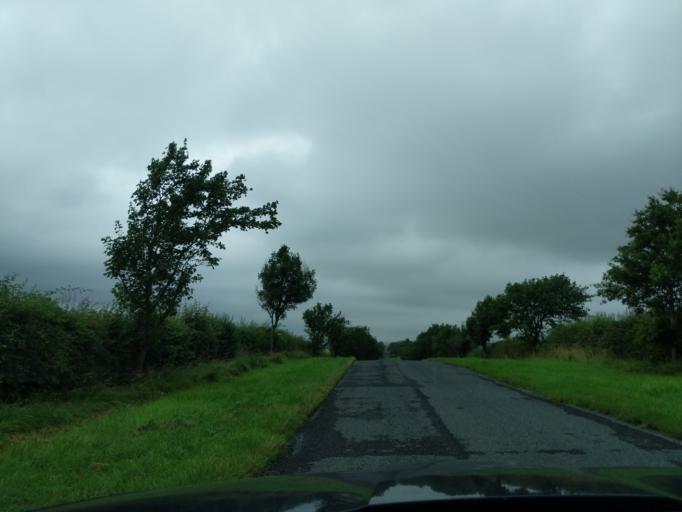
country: GB
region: England
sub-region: Northumberland
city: Ford
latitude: 55.6918
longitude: -2.1323
